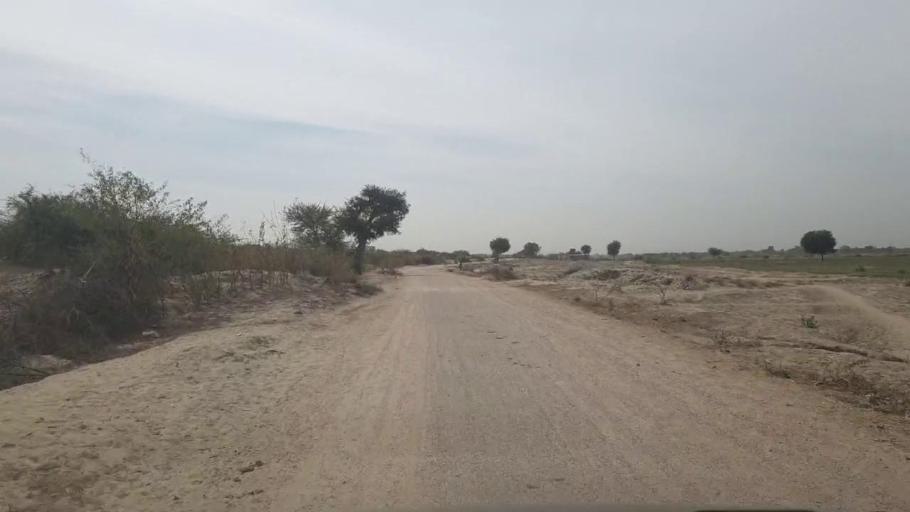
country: PK
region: Sindh
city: Umarkot
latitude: 25.2384
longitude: 69.7137
